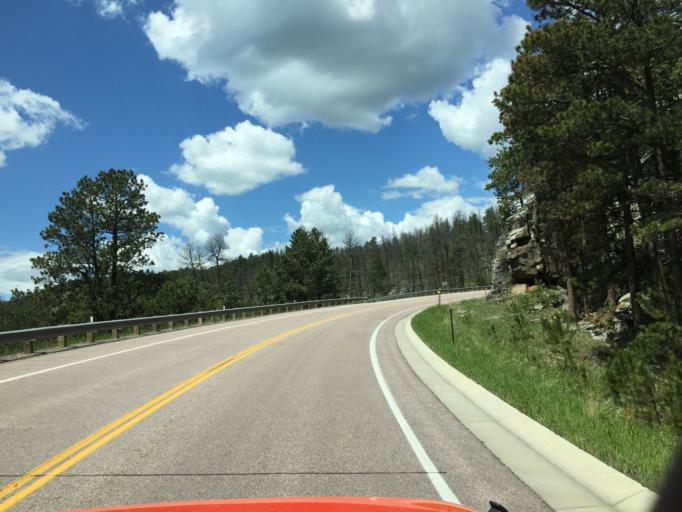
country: US
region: South Dakota
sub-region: Custer County
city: Custer
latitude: 43.8920
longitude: -103.5662
